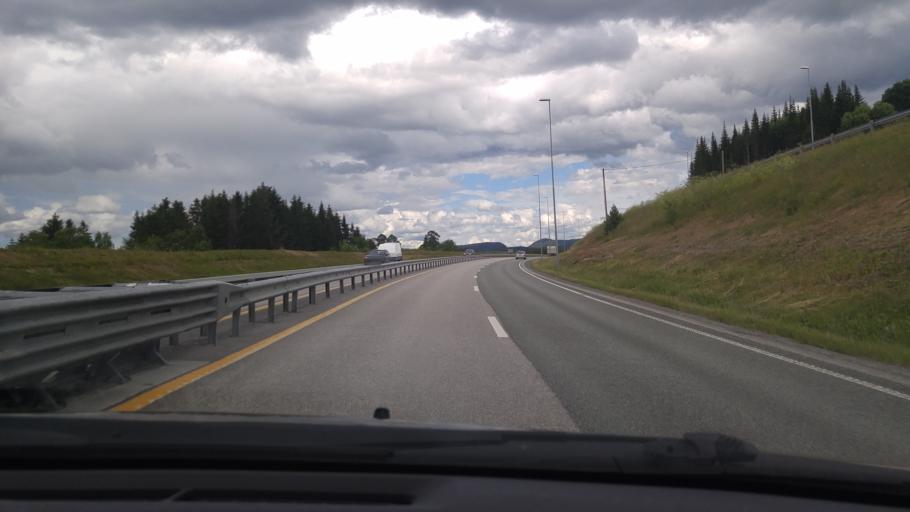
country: NO
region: Nord-Trondelag
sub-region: Steinkjer
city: Steinkjer
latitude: 63.9793
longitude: 11.4258
